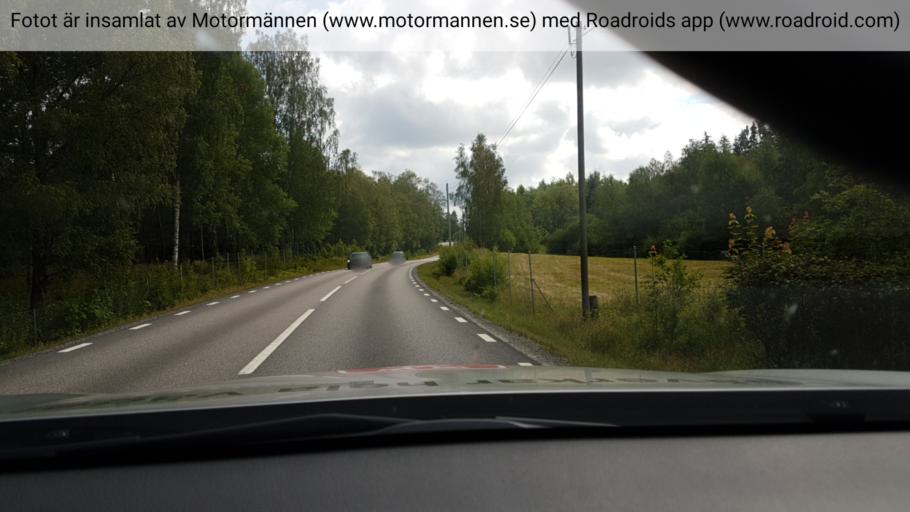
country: SE
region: Vaestra Goetaland
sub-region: Marks Kommun
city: Fritsla
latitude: 57.4817
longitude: 12.8104
